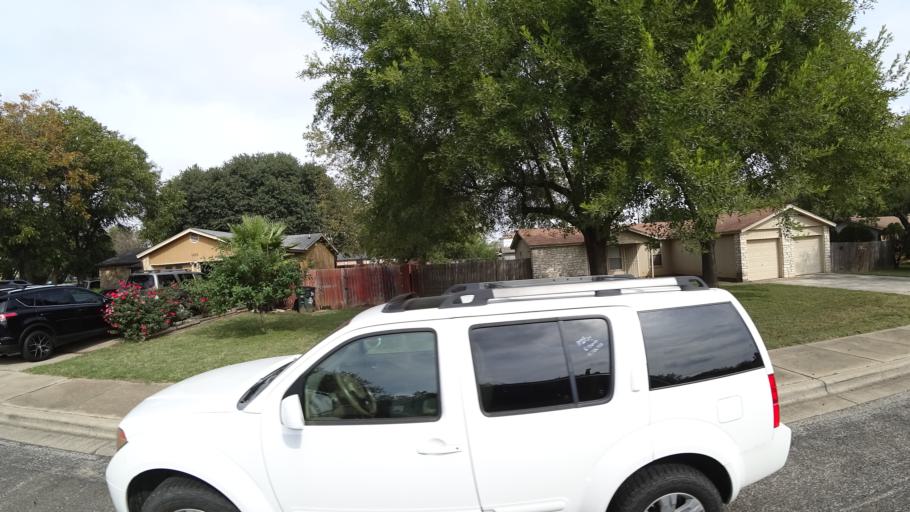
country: US
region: Texas
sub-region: Travis County
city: Wells Branch
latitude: 30.4451
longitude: -97.6619
